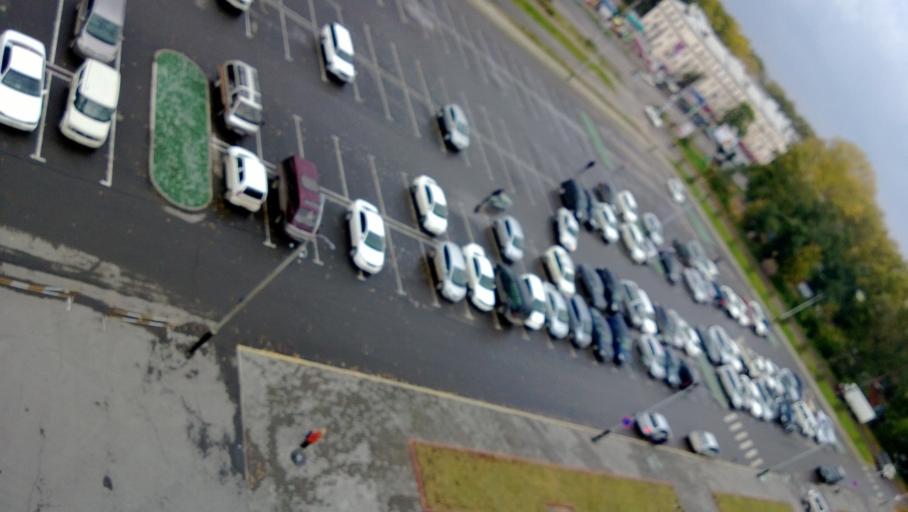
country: RU
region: Khabarovsk Krai
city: Khabarovsk Vtoroy
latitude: 48.3956
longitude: 135.1056
